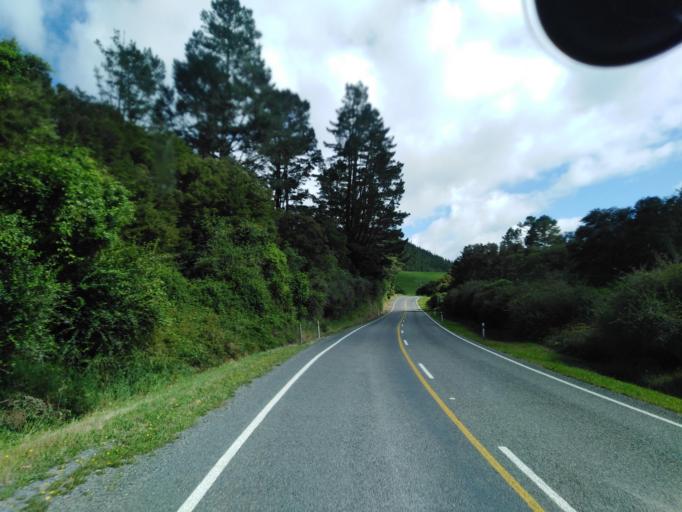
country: NZ
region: Nelson
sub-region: Nelson City
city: Nelson
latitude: -41.2904
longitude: 173.5719
